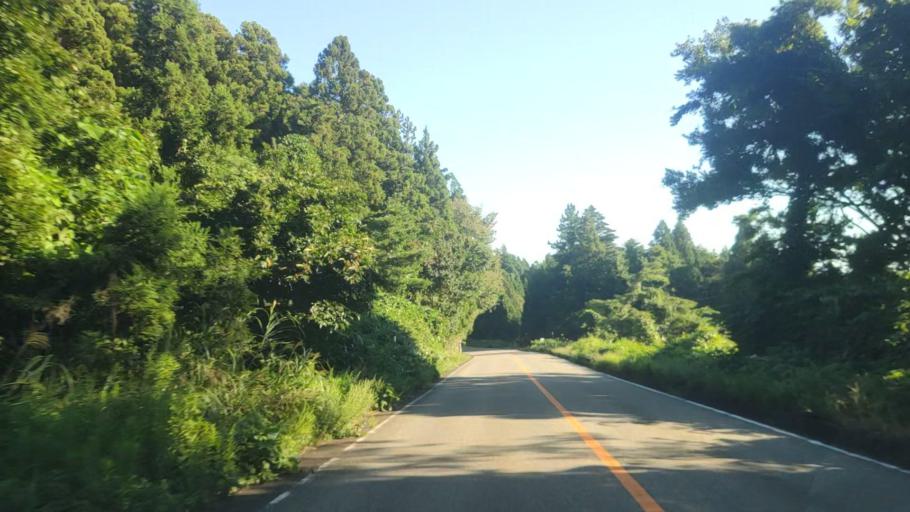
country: JP
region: Ishikawa
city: Nanao
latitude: 37.1077
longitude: 136.9461
